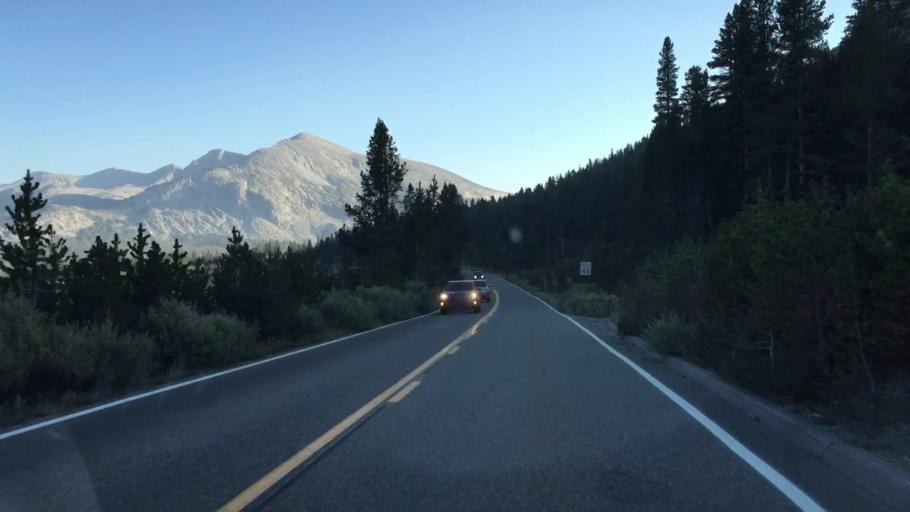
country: US
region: California
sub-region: Mono County
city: Bridgeport
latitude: 37.9070
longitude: -119.2592
